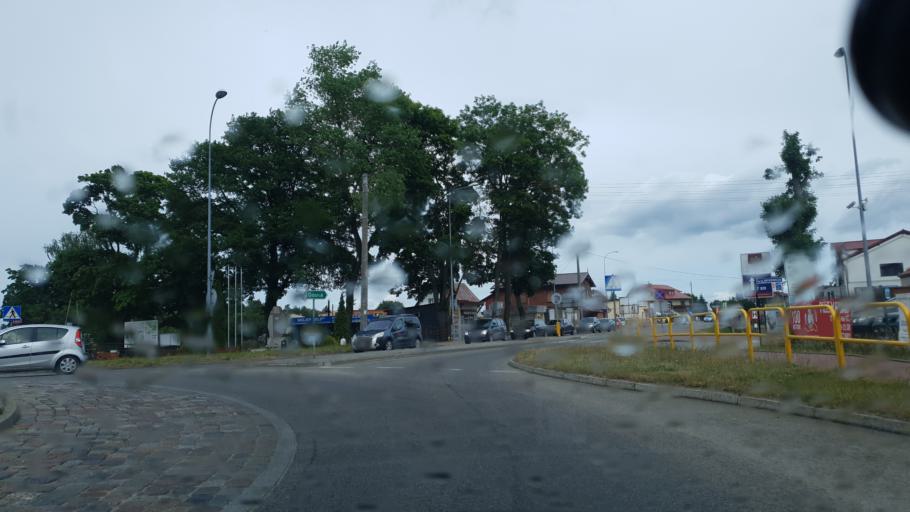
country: PL
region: Pomeranian Voivodeship
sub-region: Powiat kartuski
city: Chwaszczyno
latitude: 54.4434
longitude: 18.4189
